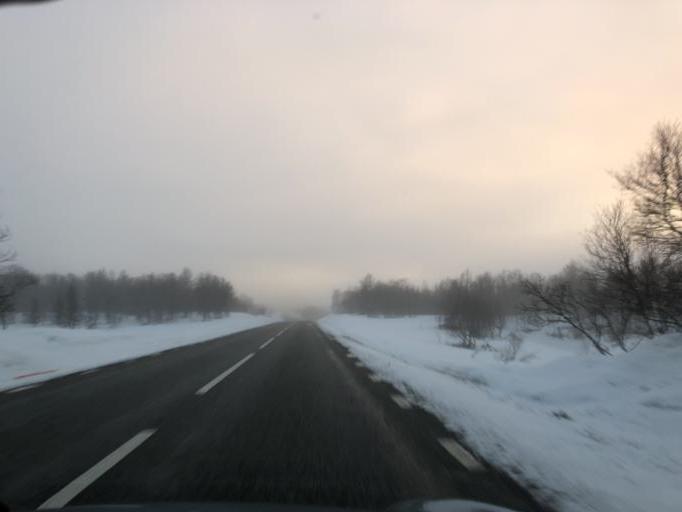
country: NO
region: Sor-Trondelag
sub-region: Tydal
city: Aas
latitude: 62.6417
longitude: 12.0899
